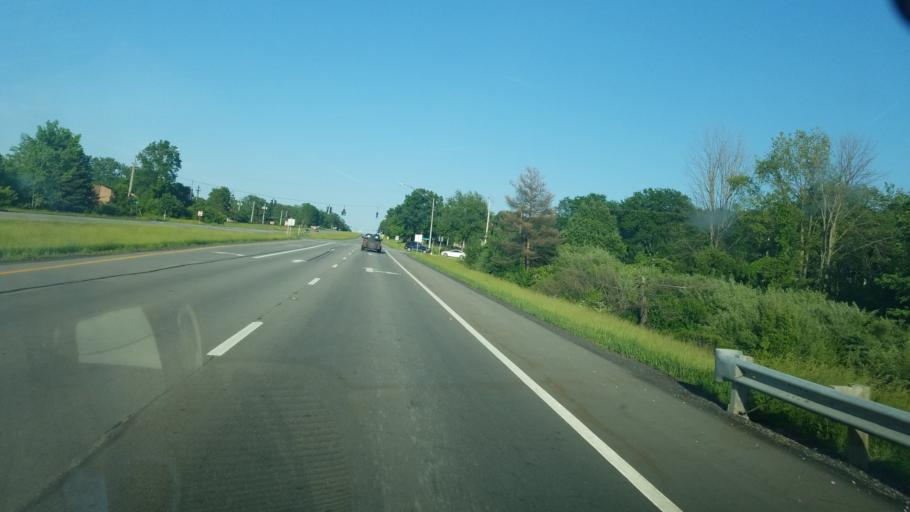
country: US
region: Ohio
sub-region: Portage County
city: Kent
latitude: 41.1344
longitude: -81.3634
